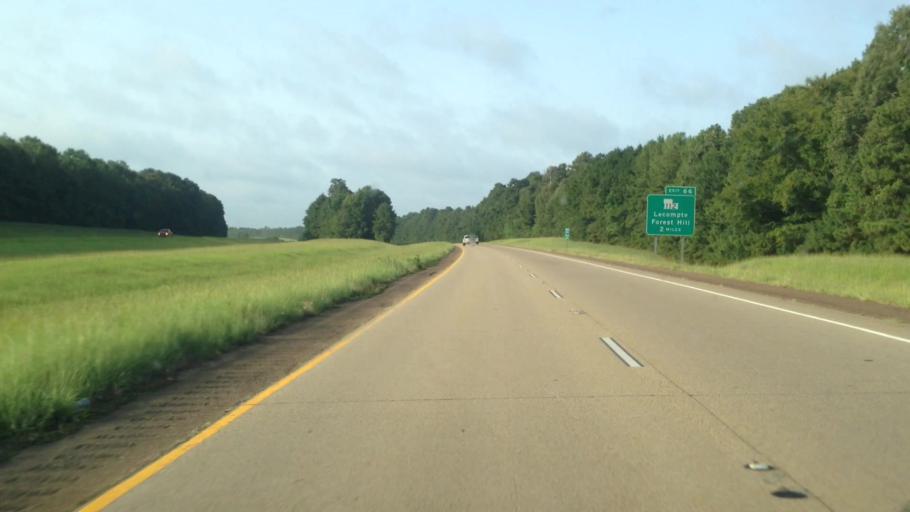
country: US
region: Louisiana
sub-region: Rapides Parish
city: Lecompte
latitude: 31.1030
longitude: -92.4454
